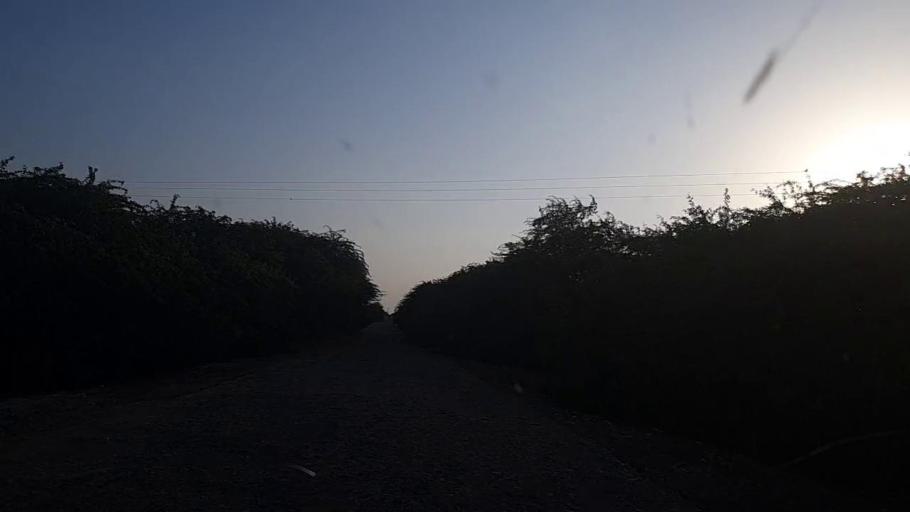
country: PK
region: Sindh
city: Khanpur
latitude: 27.6510
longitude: 69.4675
